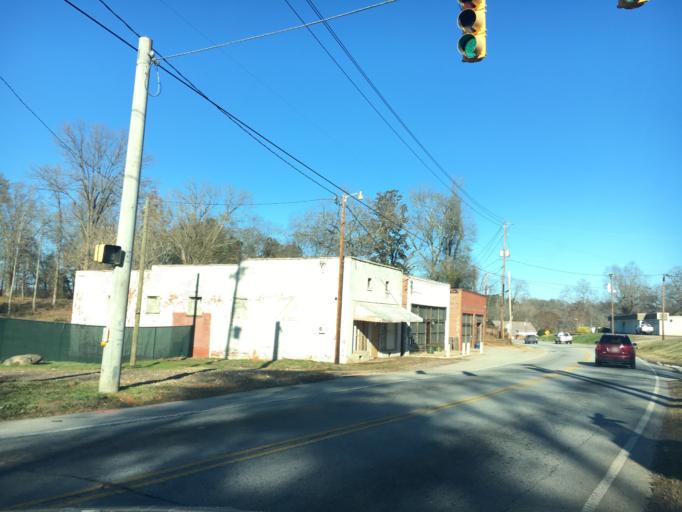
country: US
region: South Carolina
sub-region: Greenville County
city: Taylors
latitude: 34.9213
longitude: -82.2925
